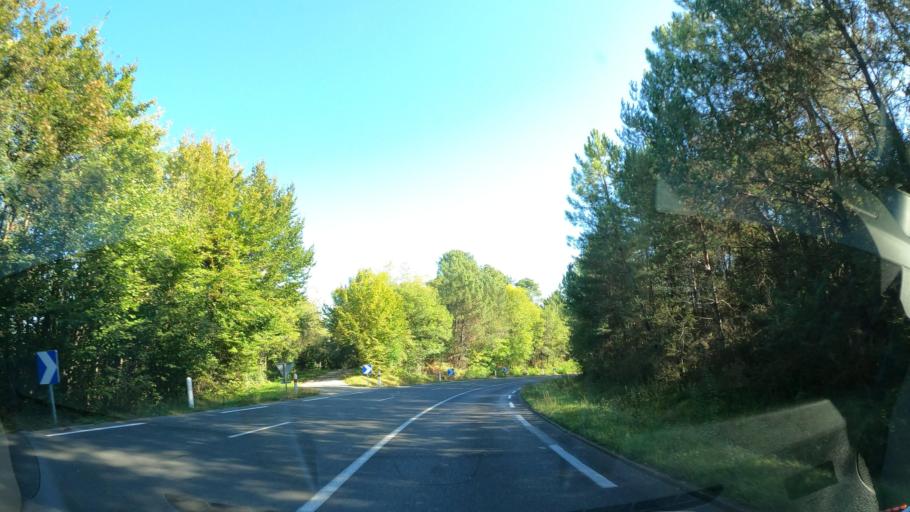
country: FR
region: Aquitaine
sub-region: Departement de la Dordogne
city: Vergt
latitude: 45.0410
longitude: 0.6468
